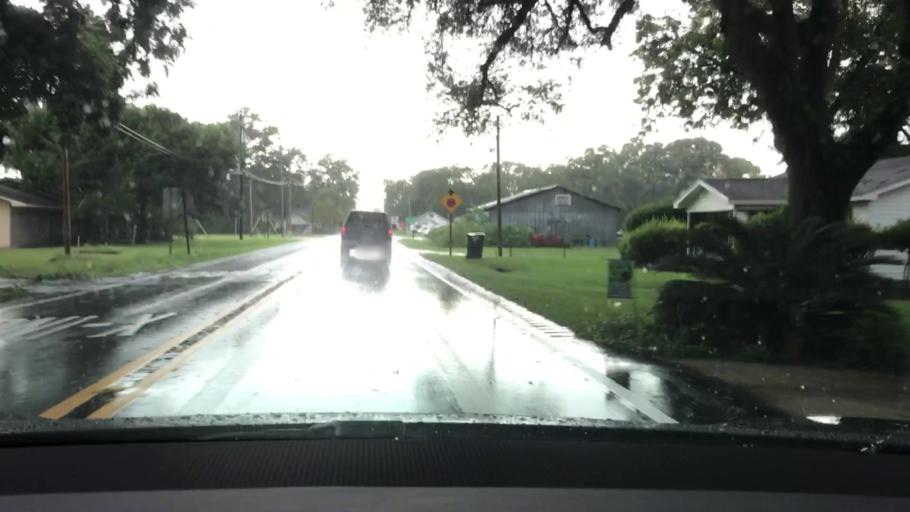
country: US
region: Alabama
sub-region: Covington County
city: Opp
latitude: 31.2165
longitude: -86.1688
